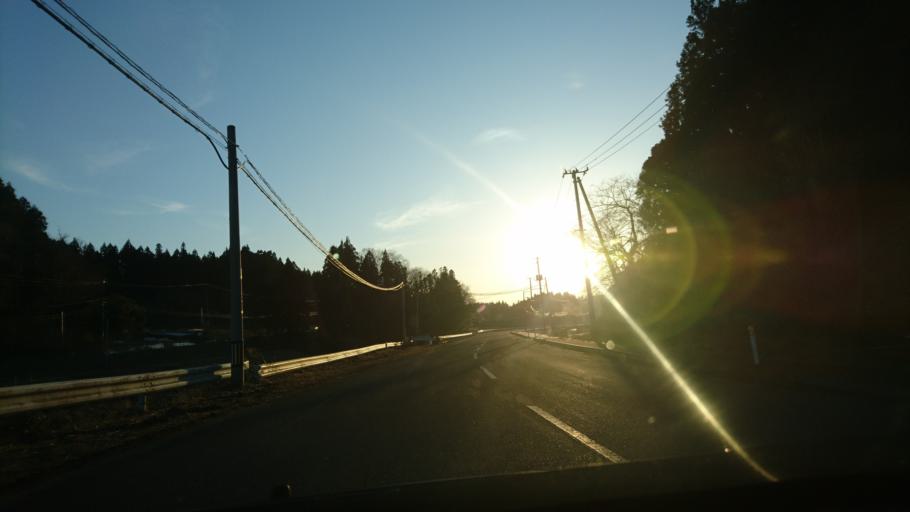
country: JP
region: Iwate
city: Mizusawa
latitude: 39.0419
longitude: 141.3522
